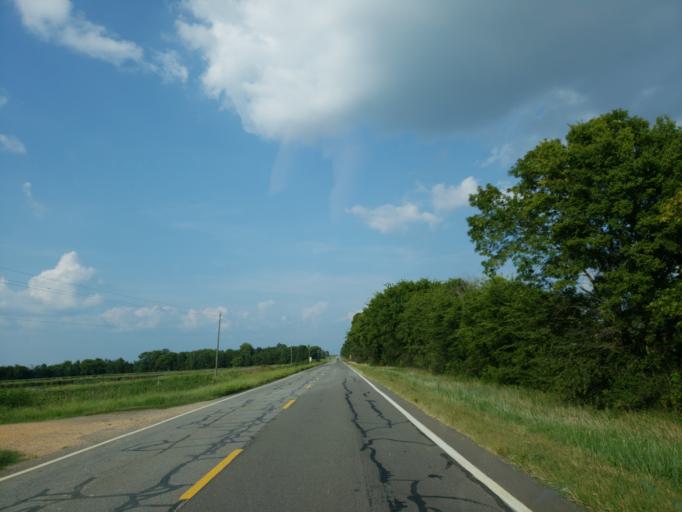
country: US
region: Alabama
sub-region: Greene County
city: Eutaw
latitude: 32.7969
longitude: -87.9658
